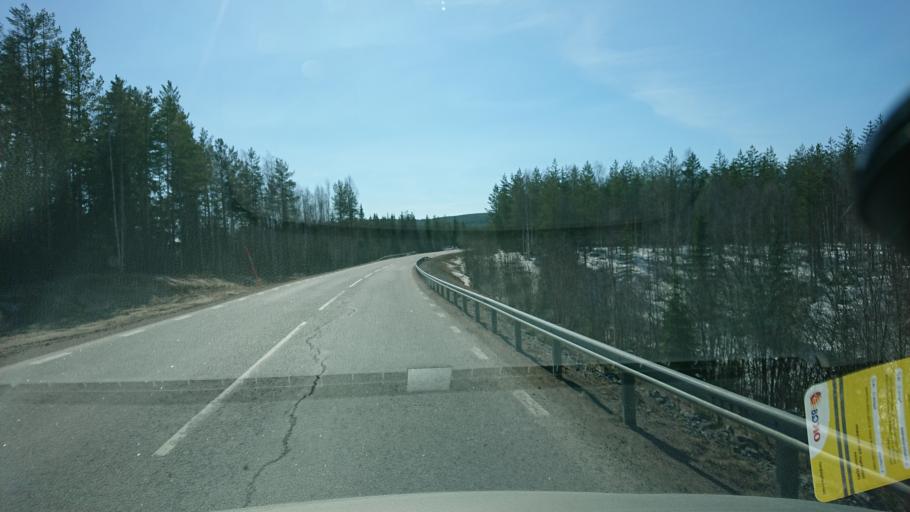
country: SE
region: Vaesternorrland
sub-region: Solleftea Kommun
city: As
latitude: 63.6419
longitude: 16.4569
